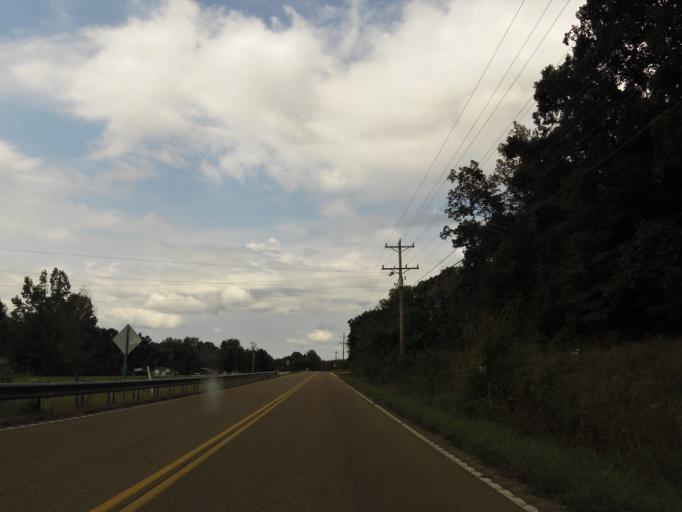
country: US
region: Tennessee
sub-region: Perry County
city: Linden
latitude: 35.6194
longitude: -87.9189
